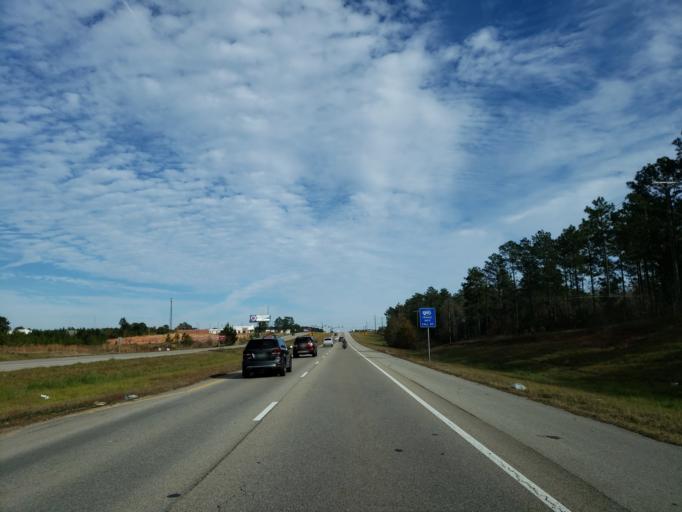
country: US
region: Mississippi
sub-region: Lamar County
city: West Hattiesburg
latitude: 31.3147
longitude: -89.4500
